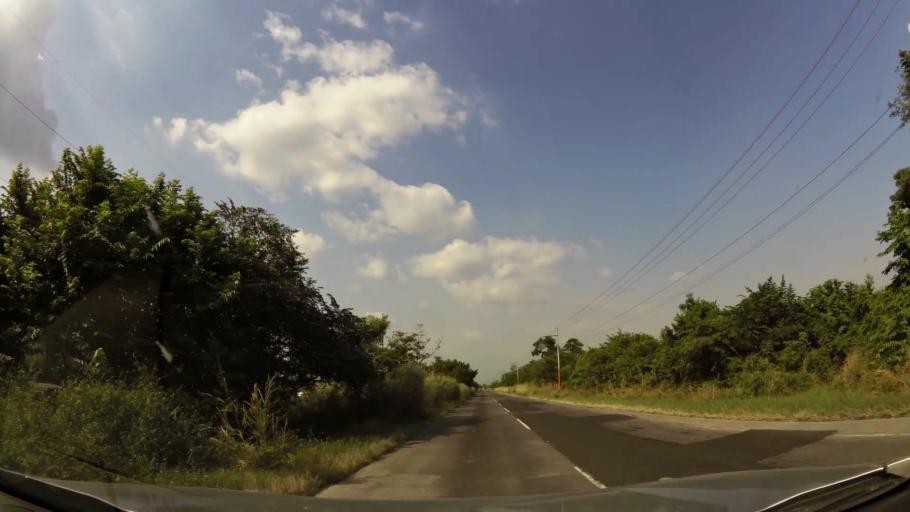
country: GT
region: Escuintla
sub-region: Municipio de Masagua
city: Masagua
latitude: 14.1149
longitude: -90.7813
